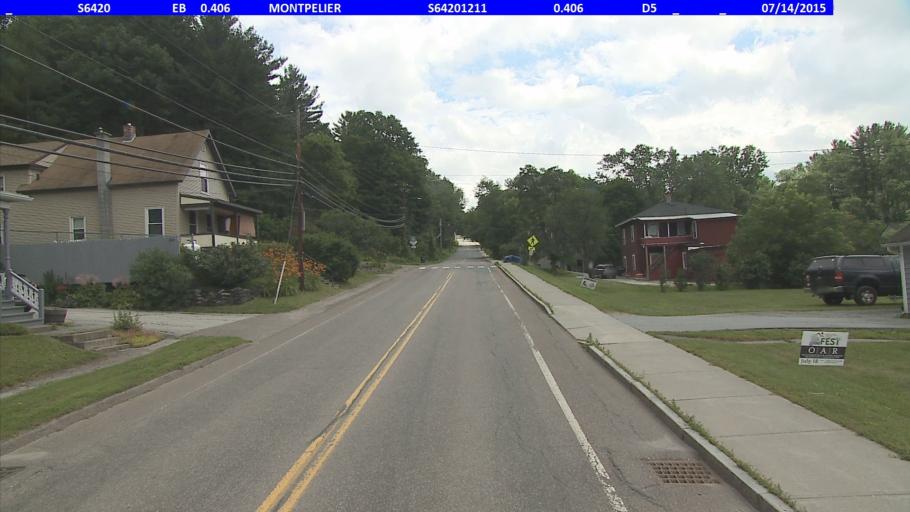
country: US
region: Vermont
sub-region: Washington County
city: Montpelier
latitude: 44.2617
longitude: -72.5650
